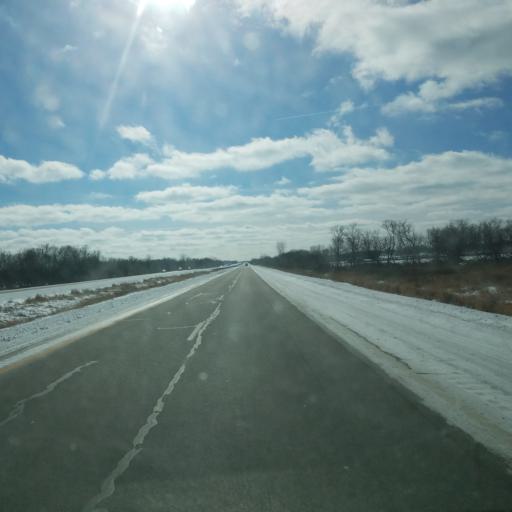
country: US
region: Michigan
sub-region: Clinton County
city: Saint Johns
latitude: 42.9774
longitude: -84.5189
